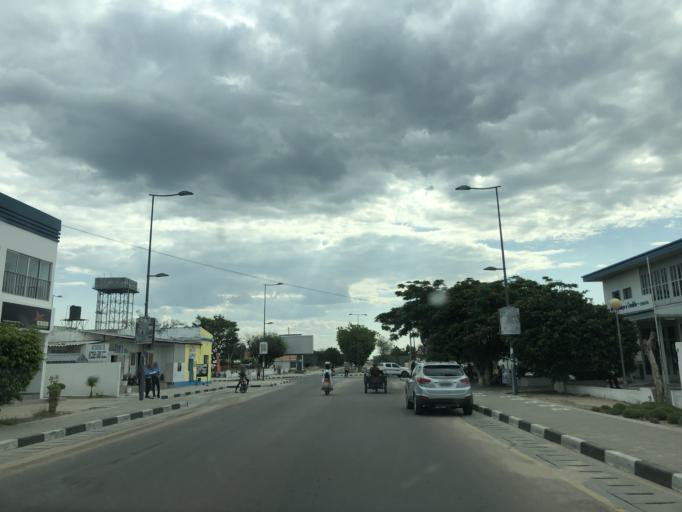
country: AO
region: Cunene
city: Ondjiva
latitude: -17.0682
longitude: 15.7226
